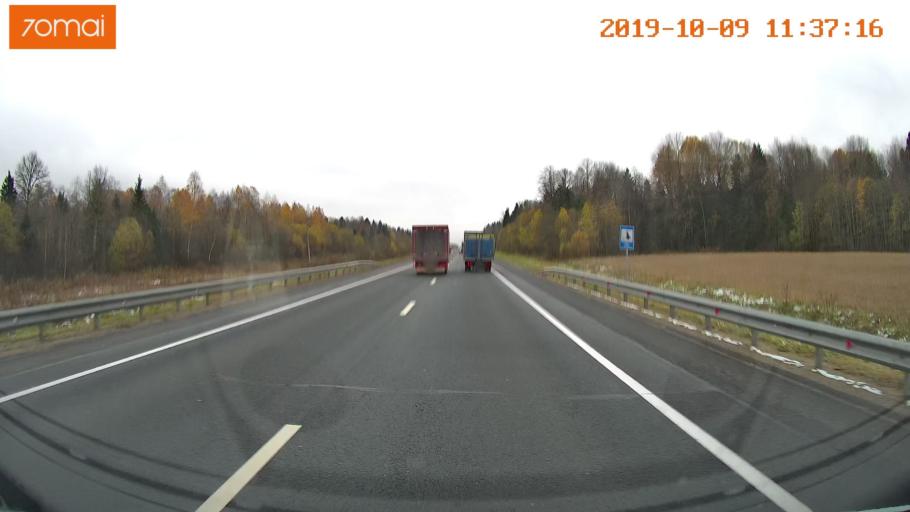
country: RU
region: Vologda
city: Gryazovets
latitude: 58.9814
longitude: 40.1446
